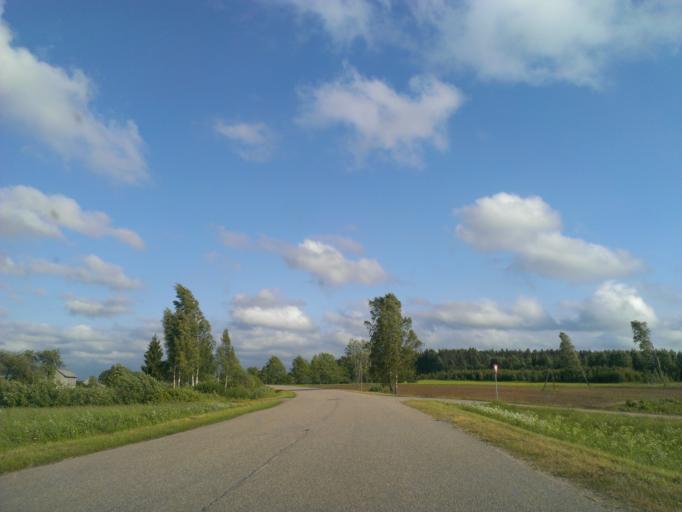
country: LV
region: Aizpute
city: Aizpute
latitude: 56.7762
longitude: 21.5205
